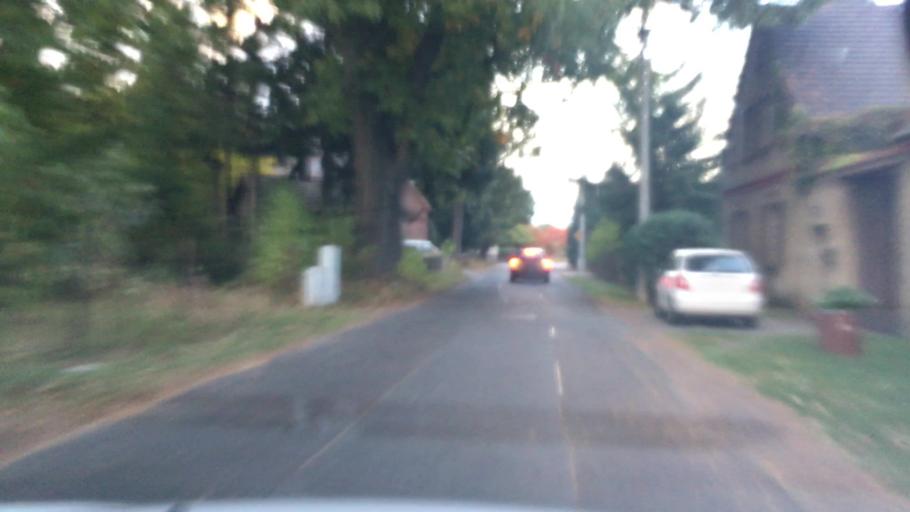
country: DE
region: Brandenburg
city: Welzow
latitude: 51.5709
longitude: 14.1696
